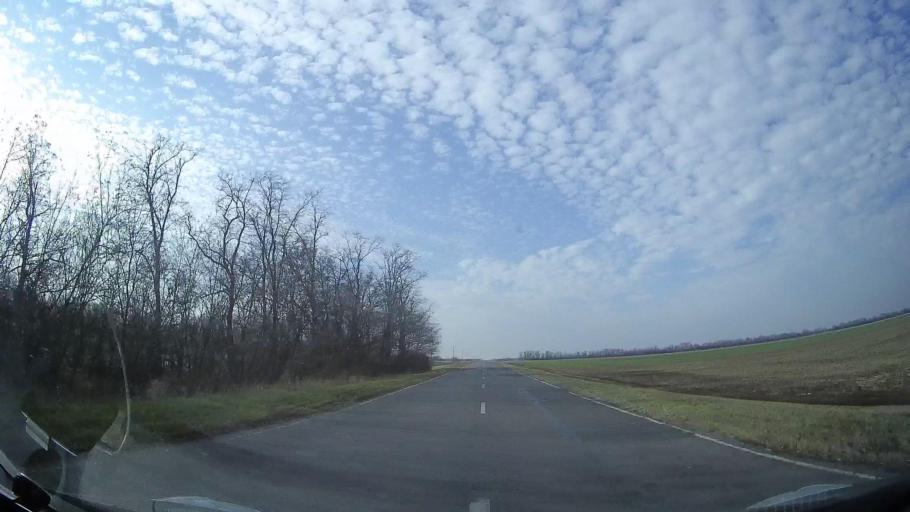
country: RU
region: Rostov
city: Veselyy
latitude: 46.9691
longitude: 40.7081
